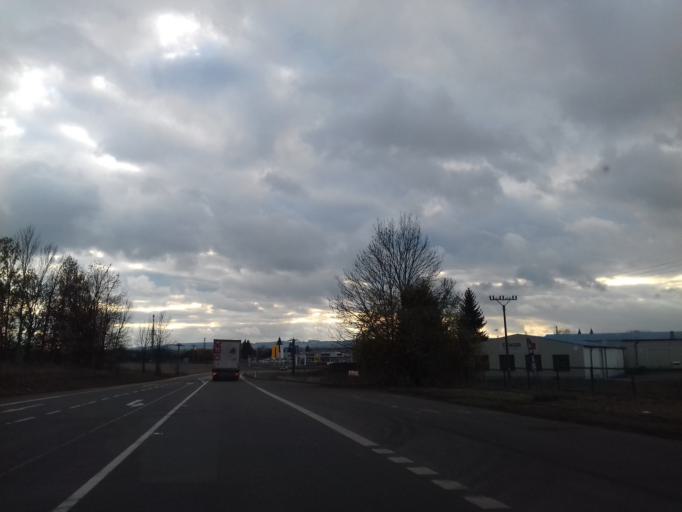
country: CZ
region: Pardubicky
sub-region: Okres Svitavy
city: Svitavy
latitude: 49.7557
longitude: 16.4842
